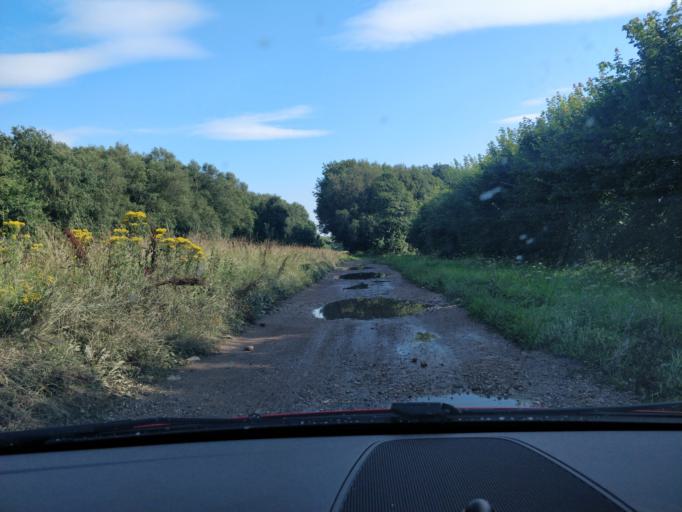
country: GB
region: England
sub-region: Lancashire
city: Banks
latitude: 53.6531
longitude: -2.8997
